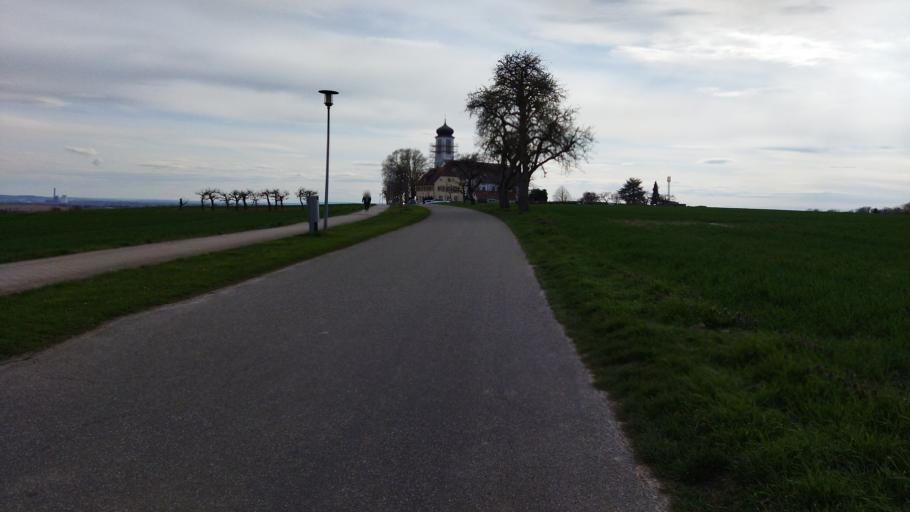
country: DE
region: Baden-Wuerttemberg
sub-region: Regierungsbezirk Stuttgart
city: Neudenau
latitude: 49.2830
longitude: 9.2205
